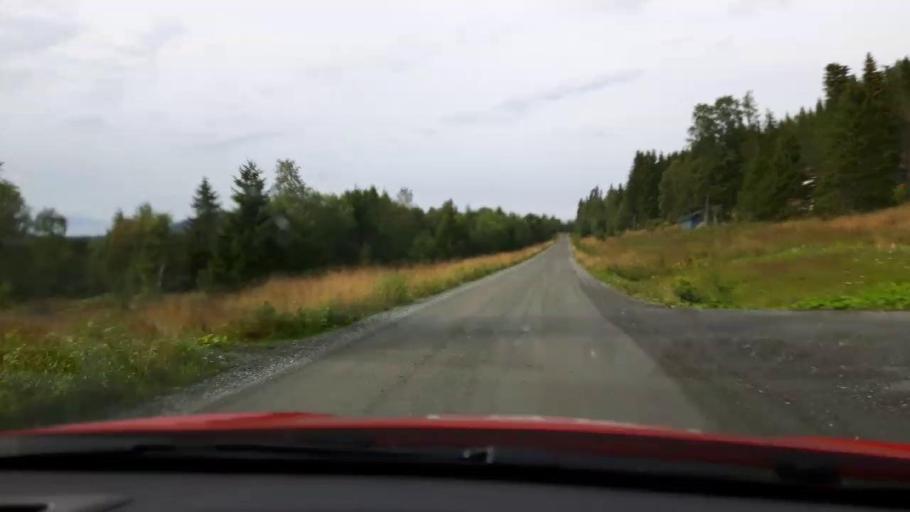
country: SE
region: Jaemtland
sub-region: Are Kommun
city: Are
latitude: 63.7451
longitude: 12.9773
